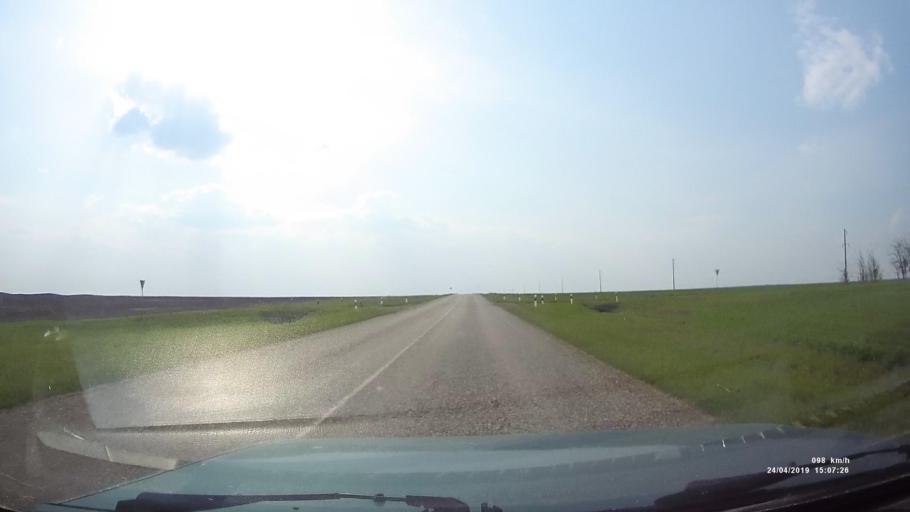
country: RU
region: Rostov
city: Remontnoye
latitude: 46.5596
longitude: 43.4050
